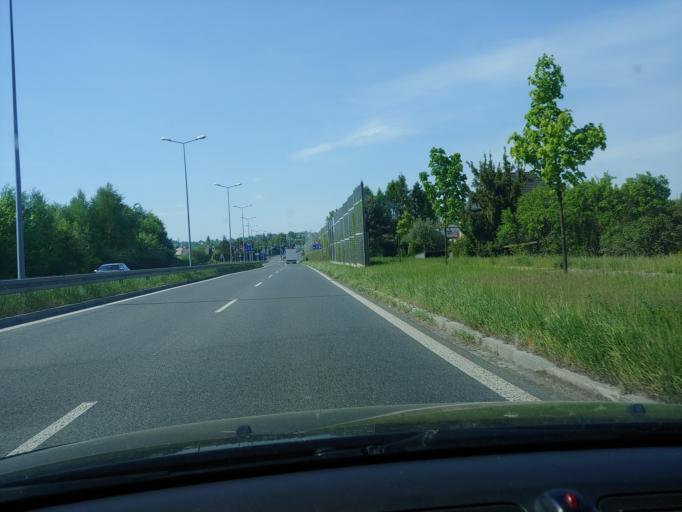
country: PL
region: Silesian Voivodeship
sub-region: Jaworzno
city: Jaworzno
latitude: 50.1782
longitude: 19.2927
